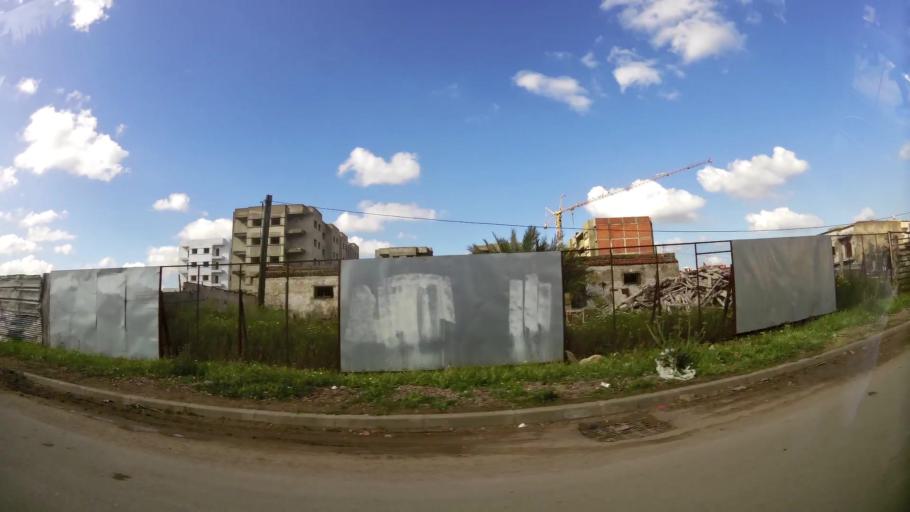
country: MA
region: Grand Casablanca
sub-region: Mediouna
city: Mediouna
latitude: 33.3874
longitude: -7.5354
